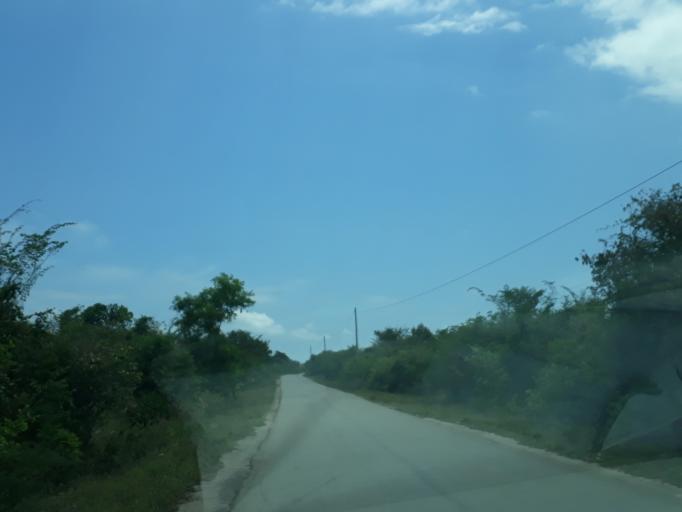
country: TZ
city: Kiwengwa
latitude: -5.9920
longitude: 39.3634
